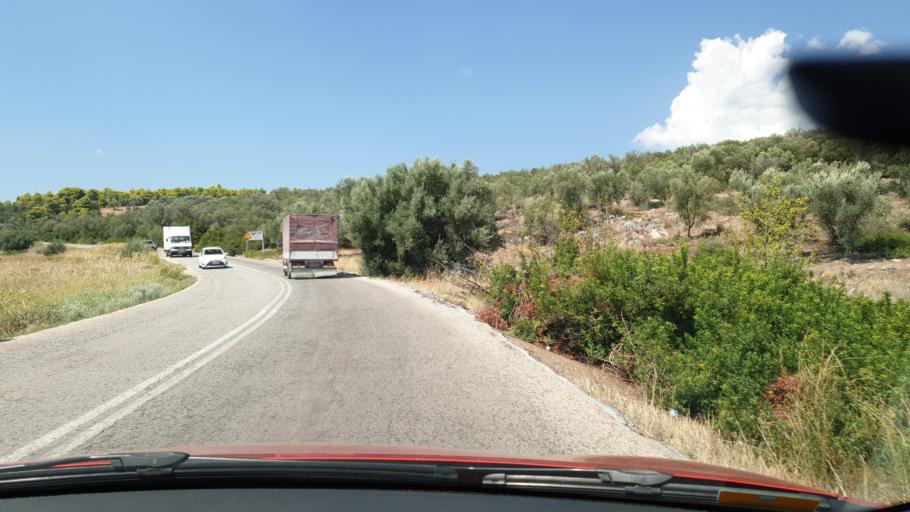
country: GR
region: Central Greece
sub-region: Nomos Evvoias
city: Psachna
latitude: 38.5870
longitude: 23.6092
